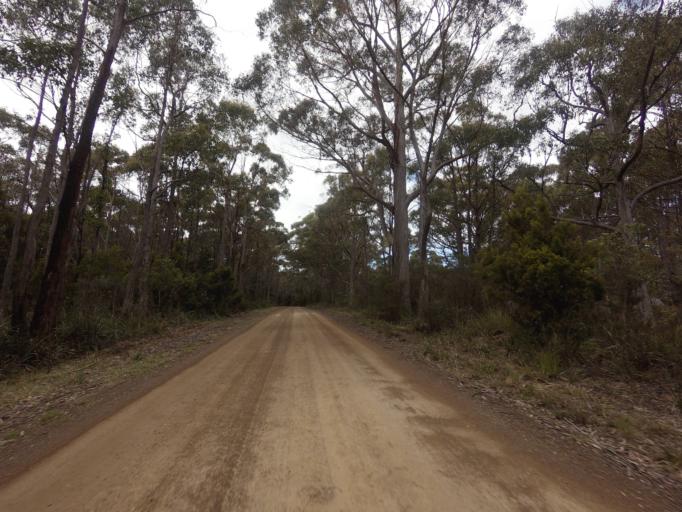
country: AU
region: Tasmania
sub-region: Huon Valley
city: Geeveston
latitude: -43.4255
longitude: 147.0037
